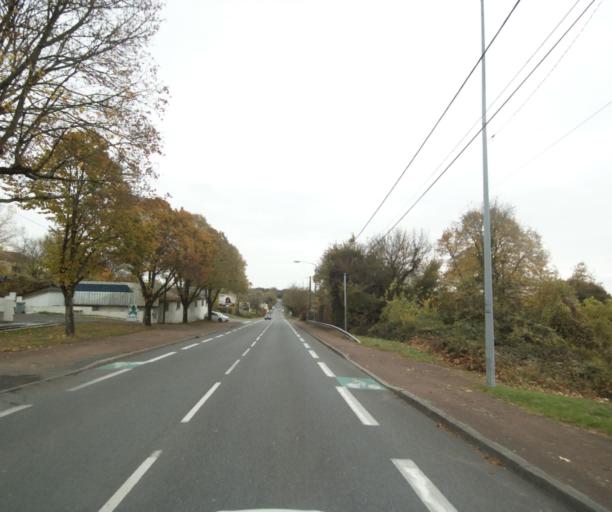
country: FR
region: Poitou-Charentes
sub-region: Departement de la Charente-Maritime
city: Saintes
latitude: 45.7301
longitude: -0.6447
